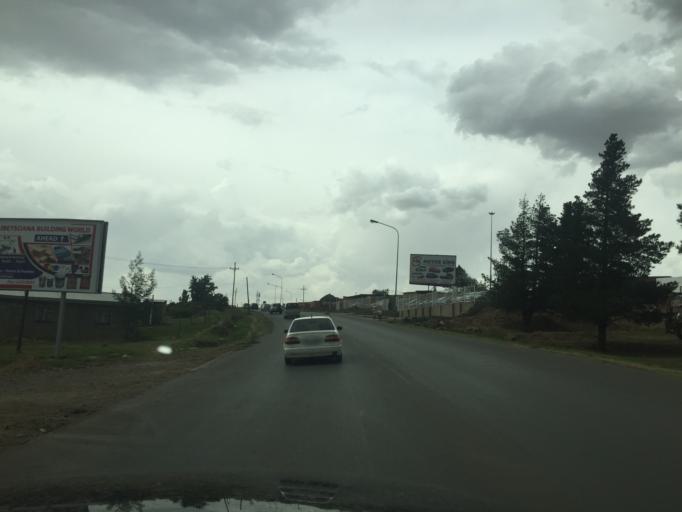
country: LS
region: Maseru
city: Maseru
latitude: -29.2977
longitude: 27.5178
